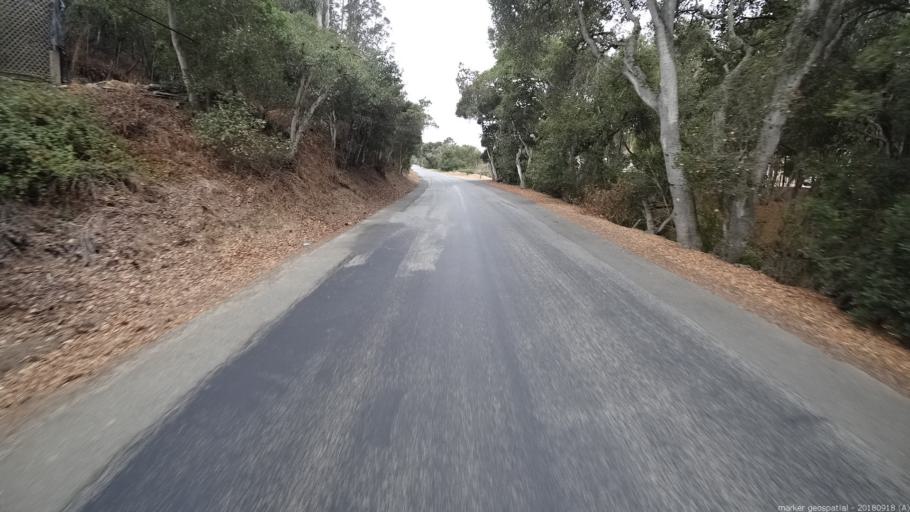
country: US
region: California
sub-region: Monterey County
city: Prunedale
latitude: 36.7820
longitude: -121.6366
